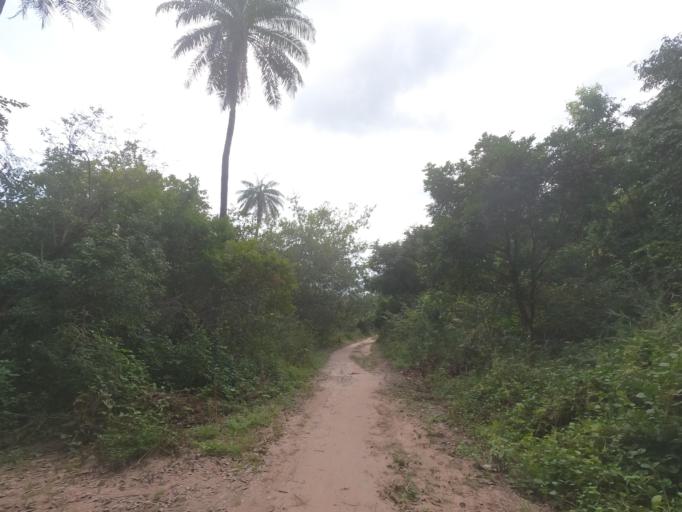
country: GW
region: Oio
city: Farim
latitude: 12.4551
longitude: -15.4098
